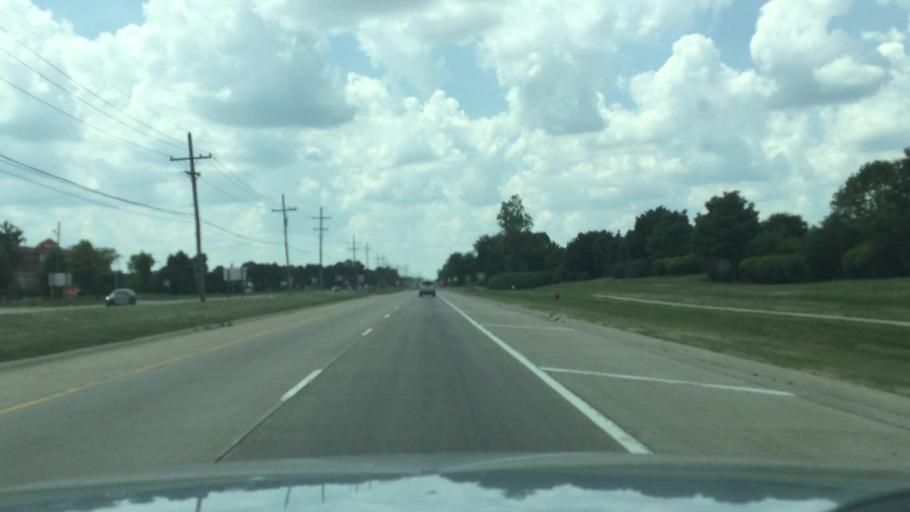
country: US
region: Michigan
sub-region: Wayne County
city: Canton
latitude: 42.2667
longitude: -83.5070
